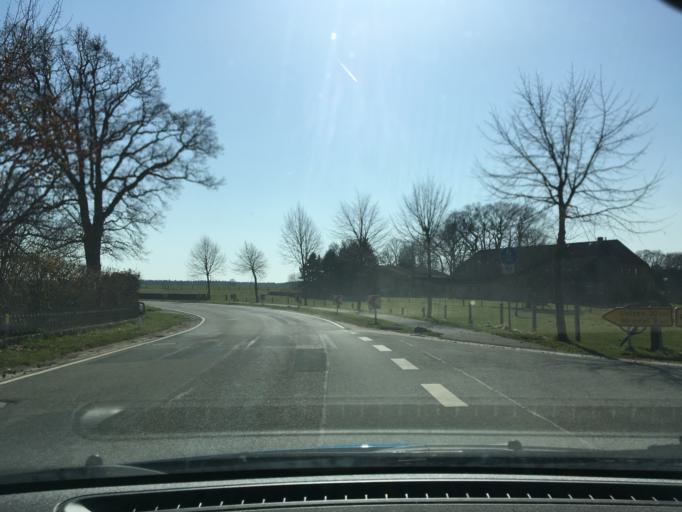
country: DE
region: Lower Saxony
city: Rehlingen
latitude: 53.0996
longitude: 10.2599
